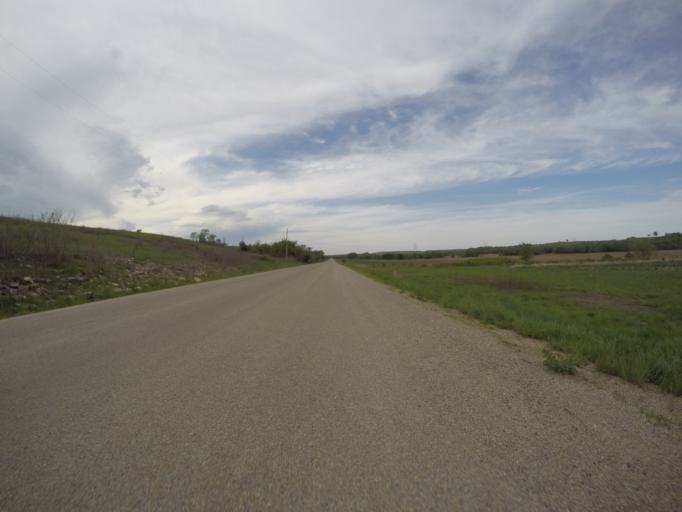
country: US
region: Kansas
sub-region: Riley County
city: Ogden
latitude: 39.0179
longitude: -96.6066
